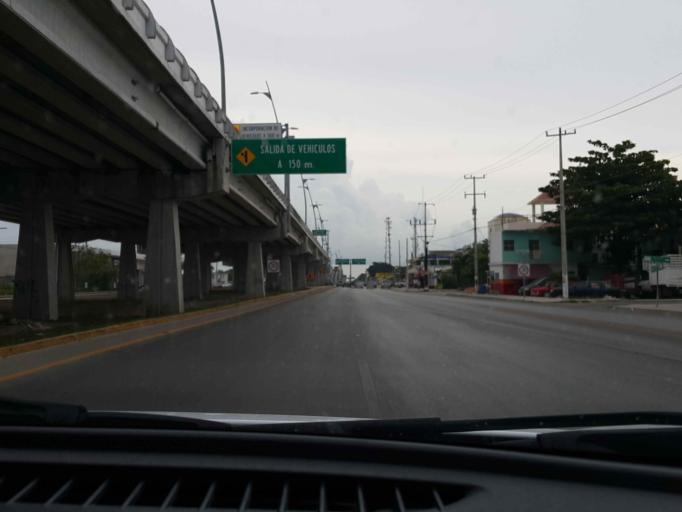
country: MX
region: Quintana Roo
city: Playa del Carmen
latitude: 20.6433
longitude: -87.0715
